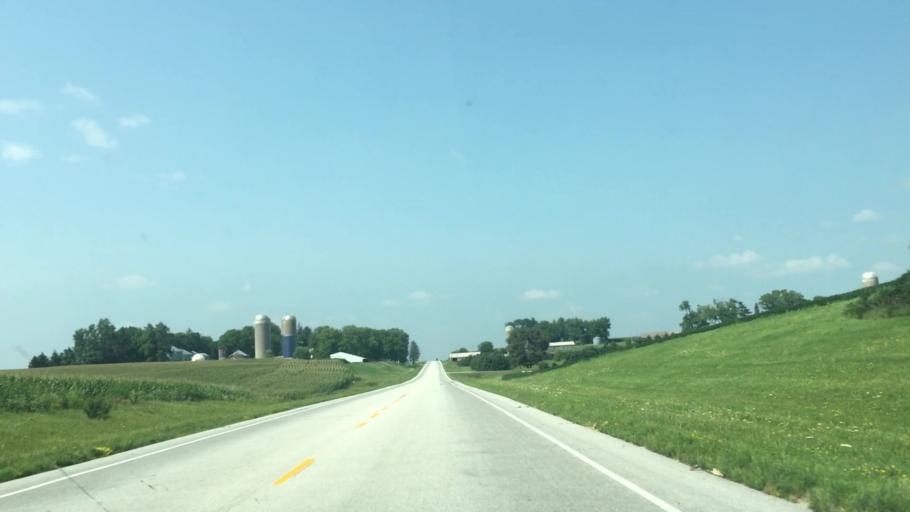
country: US
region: Minnesota
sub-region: Fillmore County
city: Harmony
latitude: 43.6114
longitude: -91.9298
